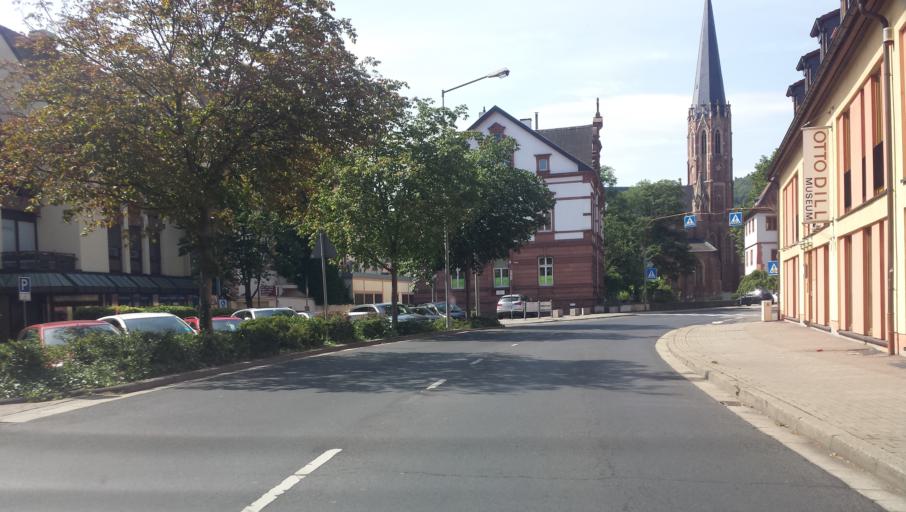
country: DE
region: Rheinland-Pfalz
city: Neustadt
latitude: 49.3544
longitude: 8.1352
